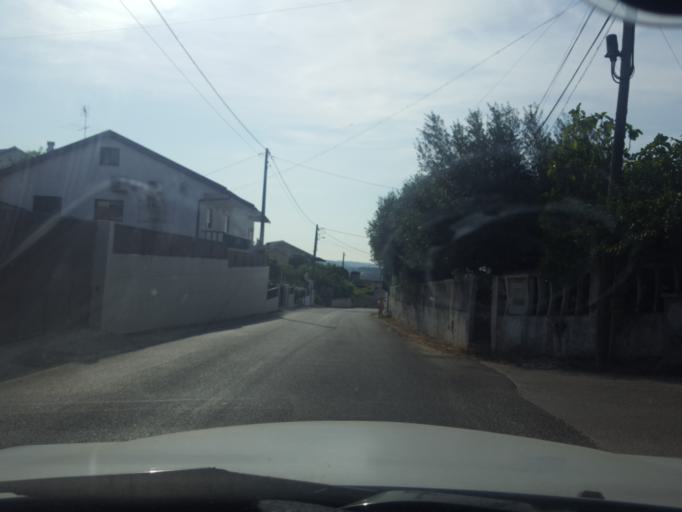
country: PT
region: Leiria
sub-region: Leiria
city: Leiria
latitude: 39.7246
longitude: -8.7775
